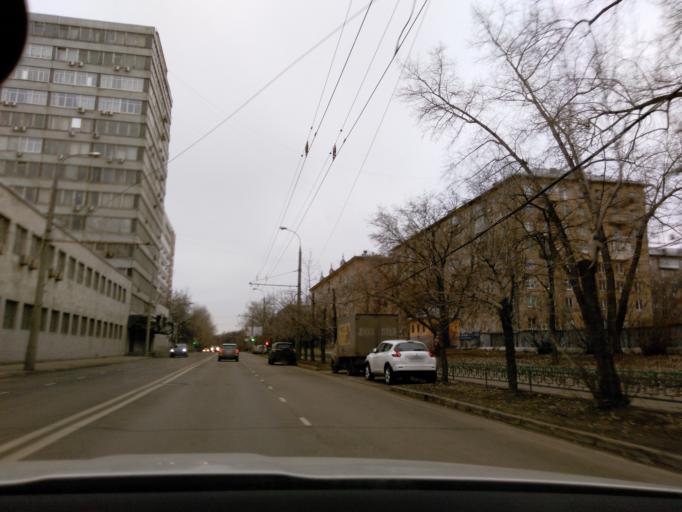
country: RU
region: Moskovskaya
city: Koptevo
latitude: 55.8157
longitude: 37.5137
